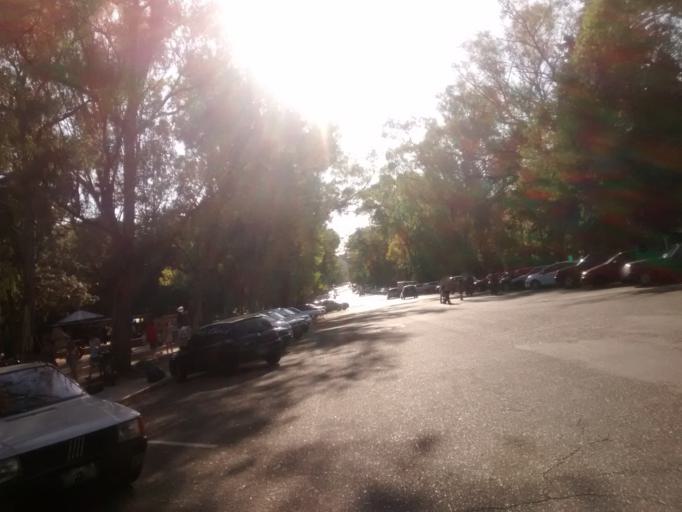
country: AR
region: Buenos Aires
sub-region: Partido de La Plata
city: La Plata
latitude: -34.9098
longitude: -57.9357
